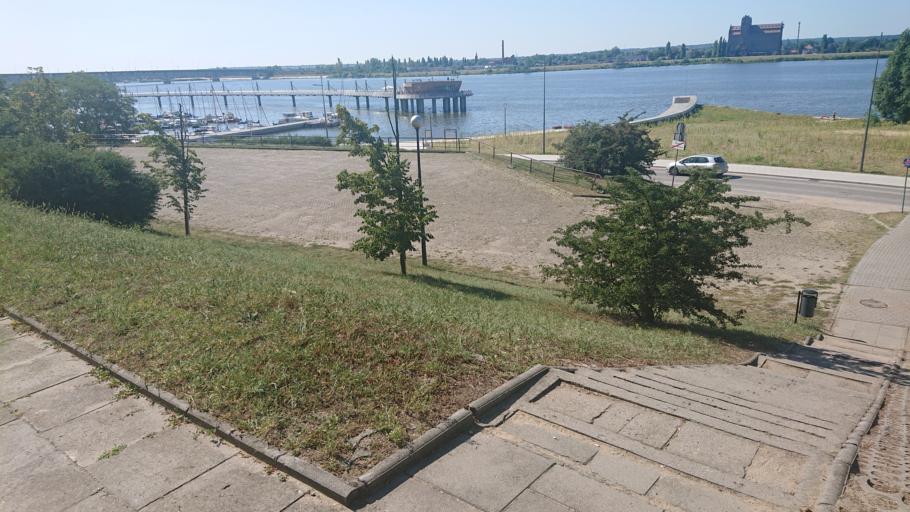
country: PL
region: Masovian Voivodeship
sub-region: Plock
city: Plock
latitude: 52.5426
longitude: 19.6844
